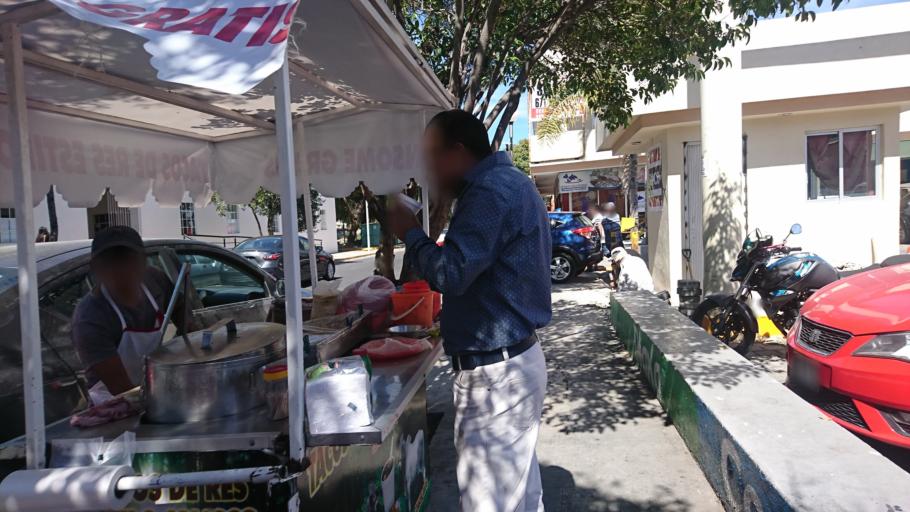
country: MX
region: Puebla
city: Tehuacan
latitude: 18.4699
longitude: -97.3929
